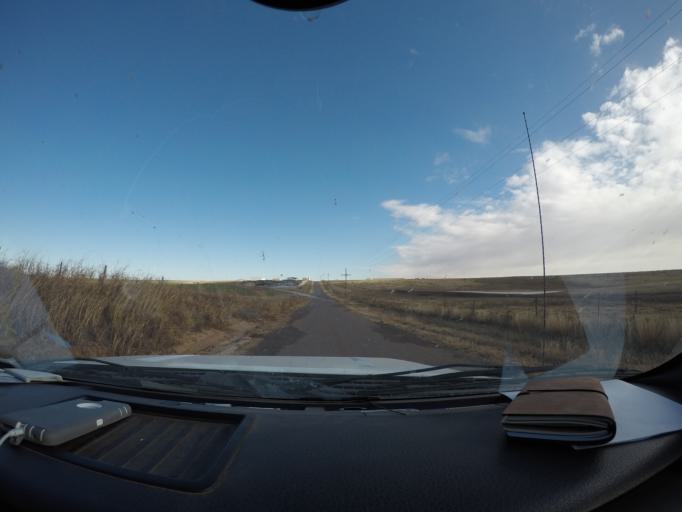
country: US
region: Texas
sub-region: Parmer County
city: Bovina
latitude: 34.6326
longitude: -103.0878
